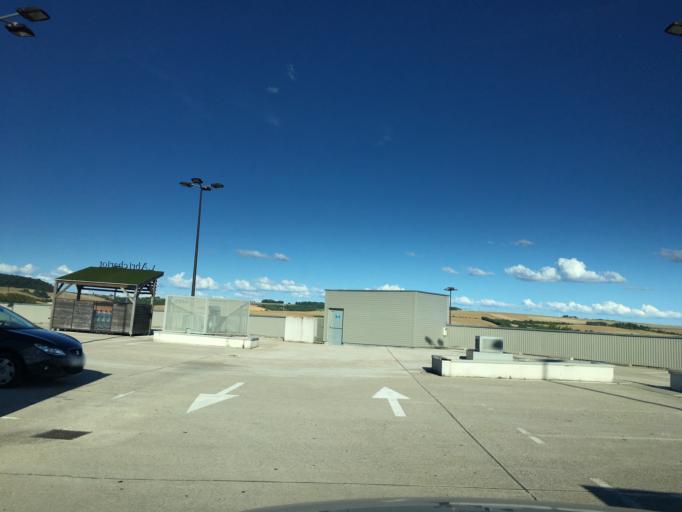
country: FR
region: Bourgogne
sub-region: Departement de l'Yonne
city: Auxerre
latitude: 47.8158
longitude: 3.5710
